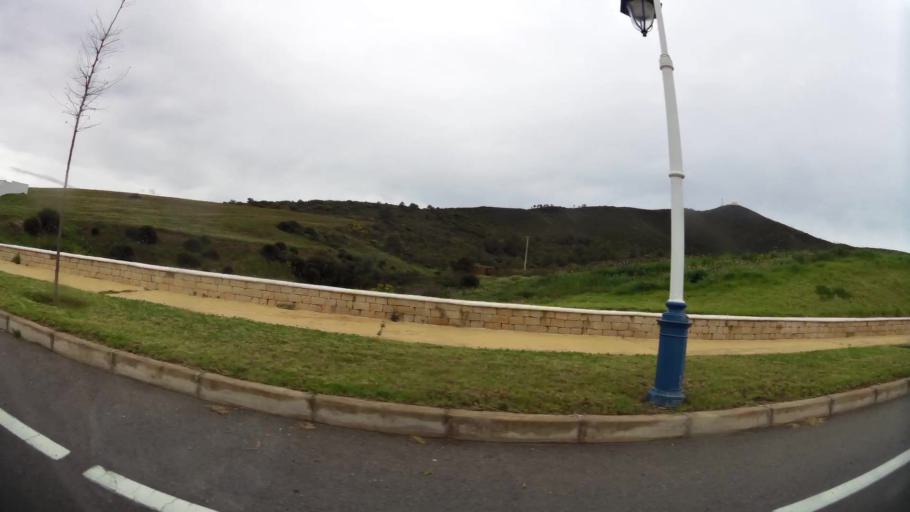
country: MA
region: Tanger-Tetouan
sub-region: Tetouan
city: Martil
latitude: 35.6667
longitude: -5.2993
